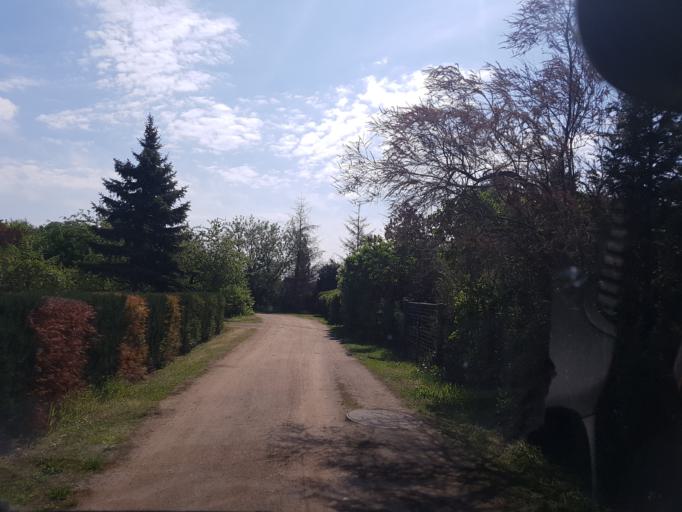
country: DE
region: Brandenburg
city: Finsterwalde
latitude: 51.6200
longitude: 13.6971
